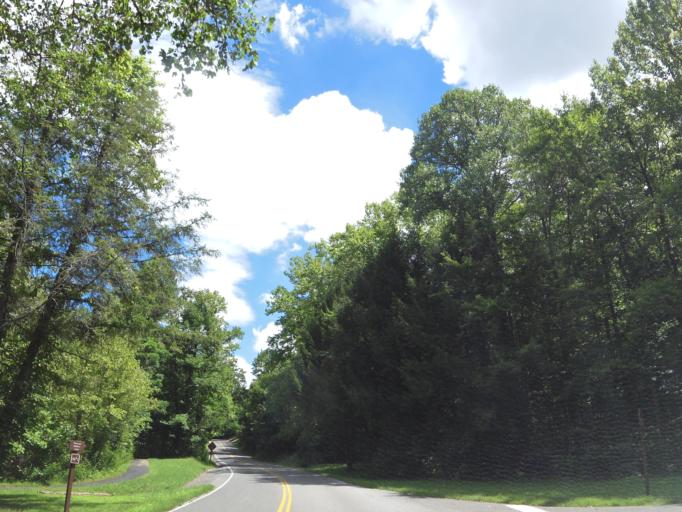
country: US
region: Kentucky
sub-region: Bell County
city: Middlesboro
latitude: 36.6036
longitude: -83.6899
